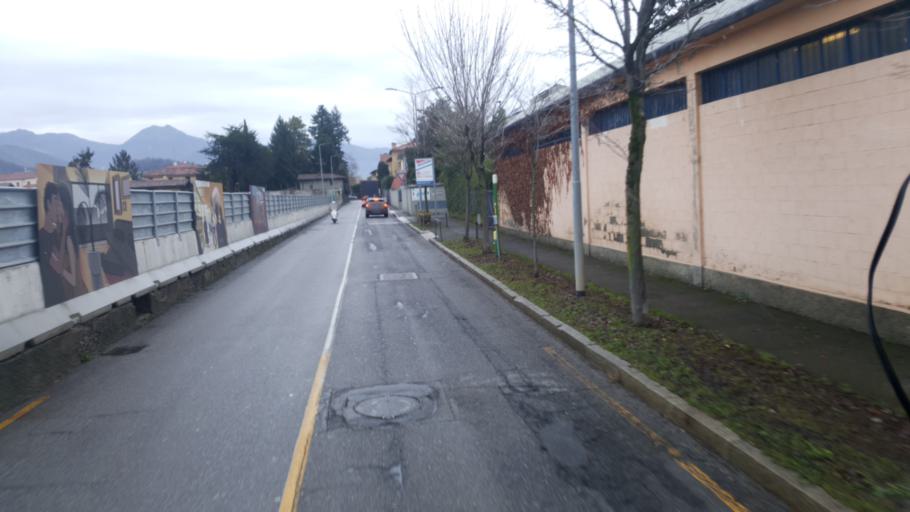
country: IT
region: Lombardy
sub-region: Provincia di Bergamo
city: Torre Boldone
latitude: 45.7033
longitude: 9.6912
